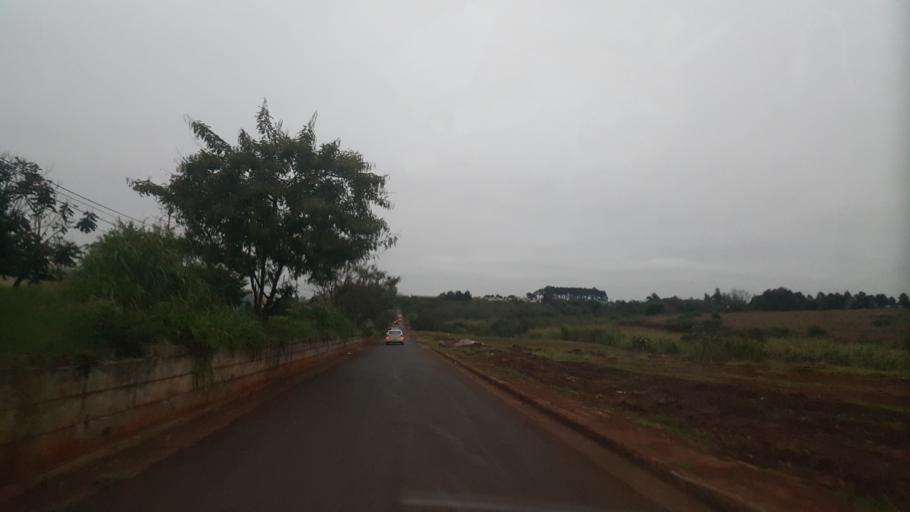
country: AR
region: Misiones
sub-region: Departamento de Capital
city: Posadas
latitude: -27.4356
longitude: -55.9174
